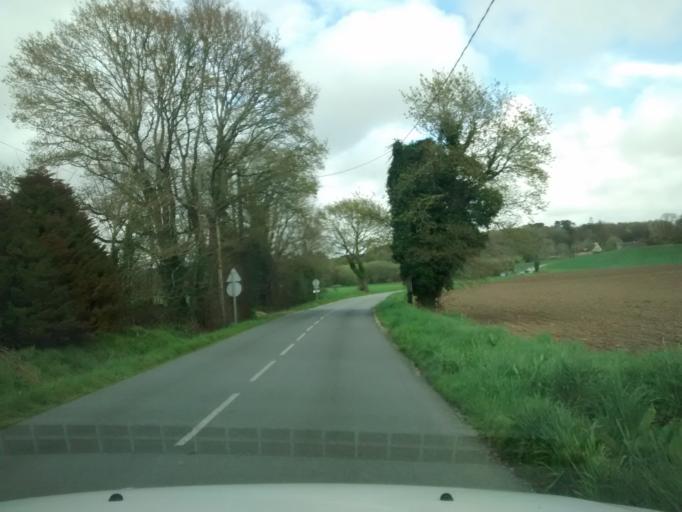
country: FR
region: Brittany
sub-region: Departement du Morbihan
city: Gestel
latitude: 47.7843
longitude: -3.4727
